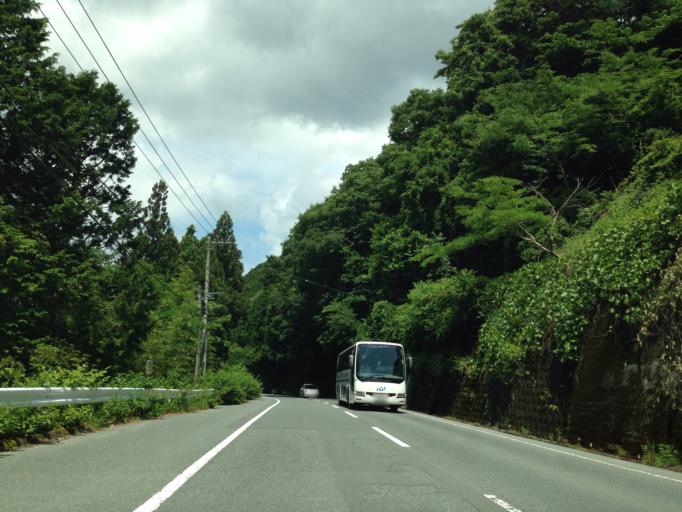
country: JP
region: Shizuoka
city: Heda
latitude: 34.9113
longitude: 138.8946
